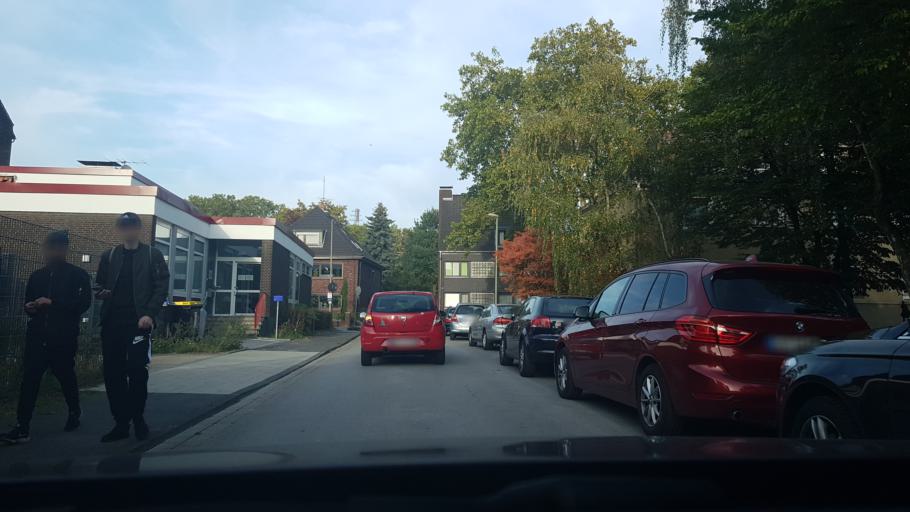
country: DE
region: North Rhine-Westphalia
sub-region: Regierungsbezirk Dusseldorf
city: Hochfeld
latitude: 51.4107
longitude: 6.7240
